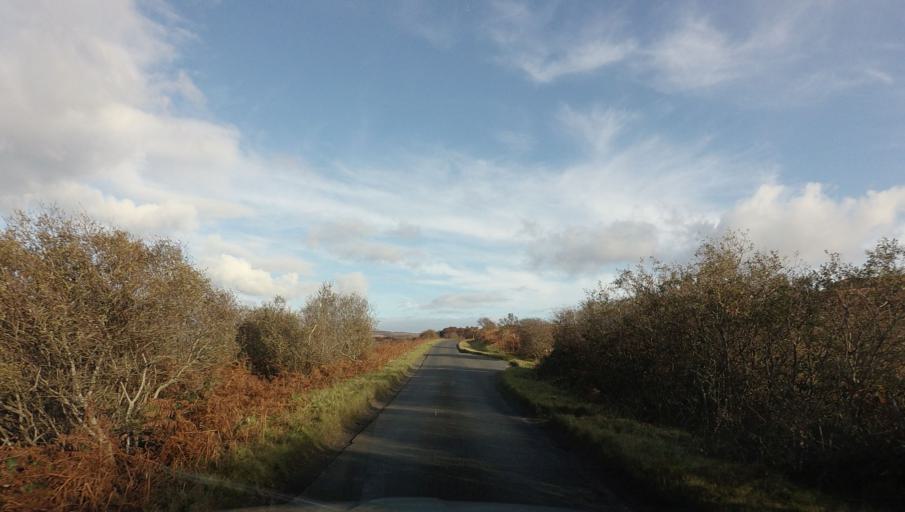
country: GB
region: Scotland
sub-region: Argyll and Bute
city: Isle Of Mull
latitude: 56.3436
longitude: -6.1175
